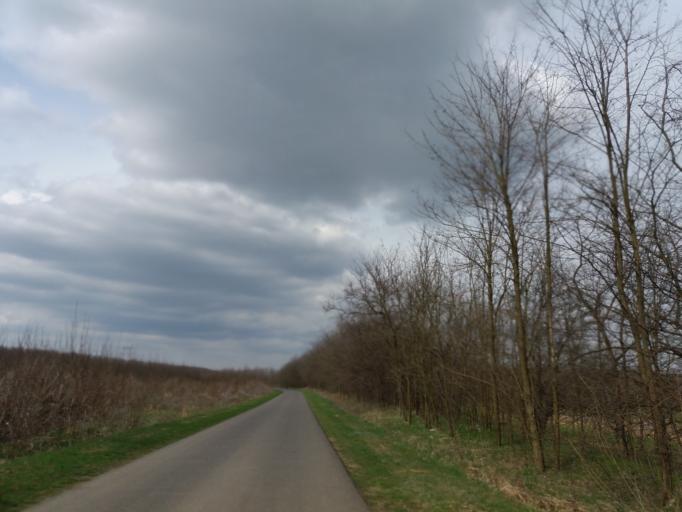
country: HU
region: Szabolcs-Szatmar-Bereg
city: Petnehaza
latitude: 48.0675
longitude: 22.0461
